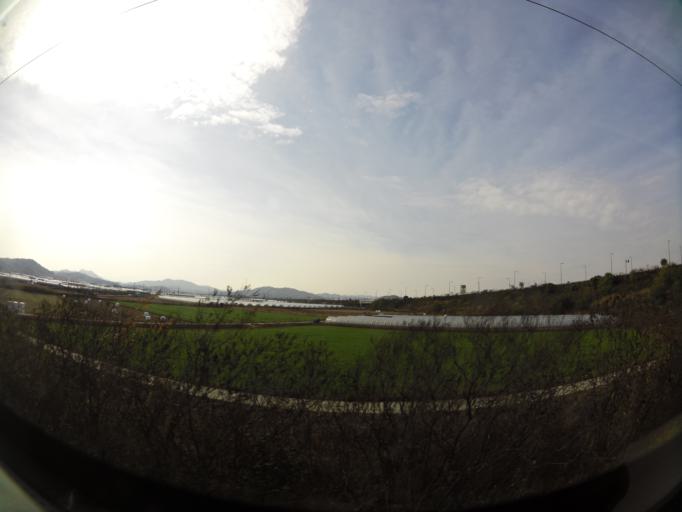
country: KR
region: Daejeon
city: Songgang-dong
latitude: 36.5694
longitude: 127.3162
